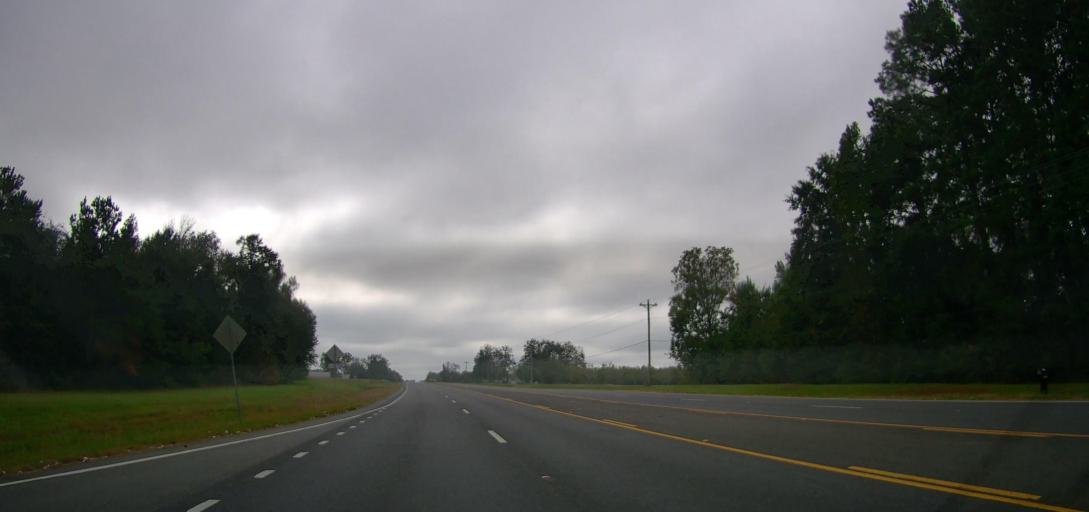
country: US
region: Georgia
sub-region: Thomas County
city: Thomasville
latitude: 30.9679
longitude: -83.8920
